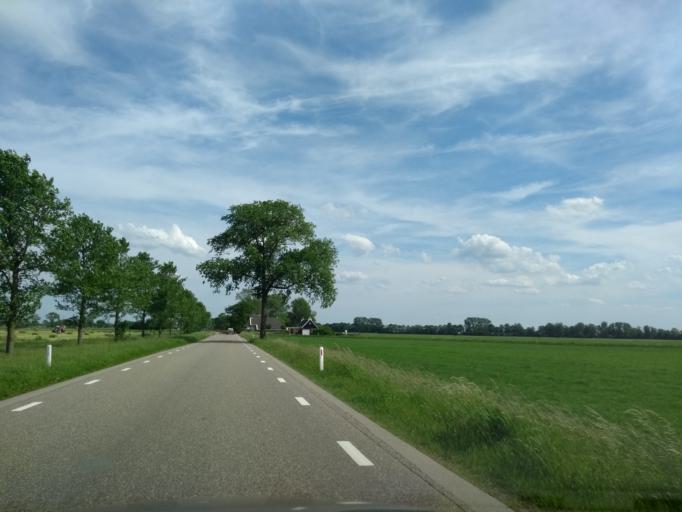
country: NL
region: Groningen
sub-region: Gemeente Zuidhorn
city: Aduard
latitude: 53.2680
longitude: 6.4367
